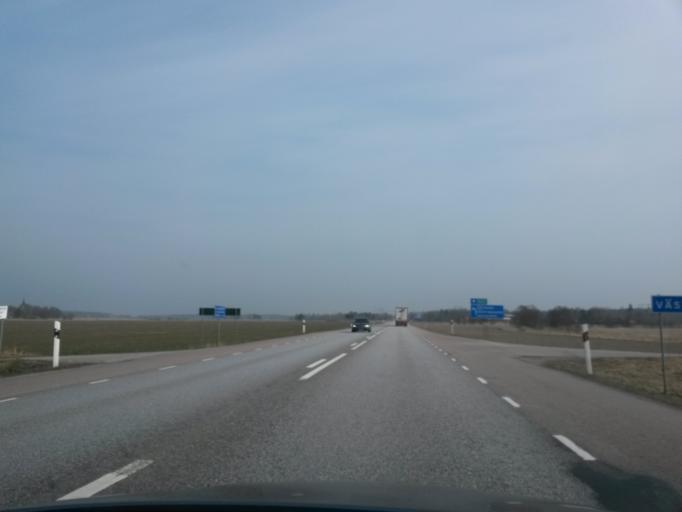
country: SE
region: Vaestra Goetaland
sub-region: Mariestads Kommun
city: Mariestad
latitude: 58.7422
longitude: 13.9427
